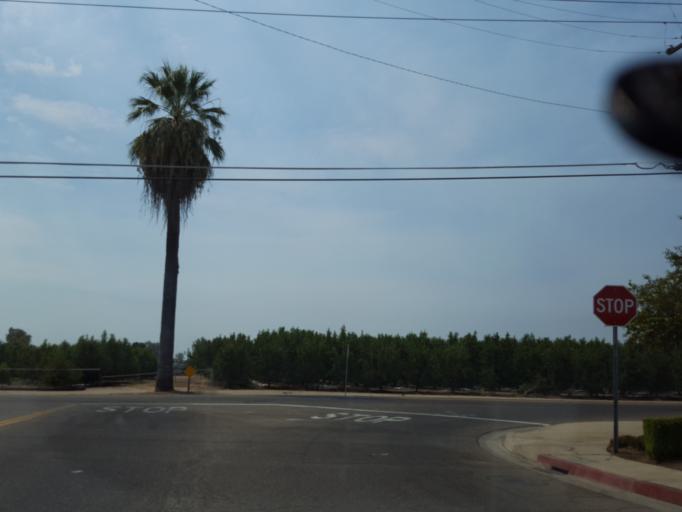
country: US
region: California
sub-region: Fresno County
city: Reedley
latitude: 36.6115
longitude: -119.4568
